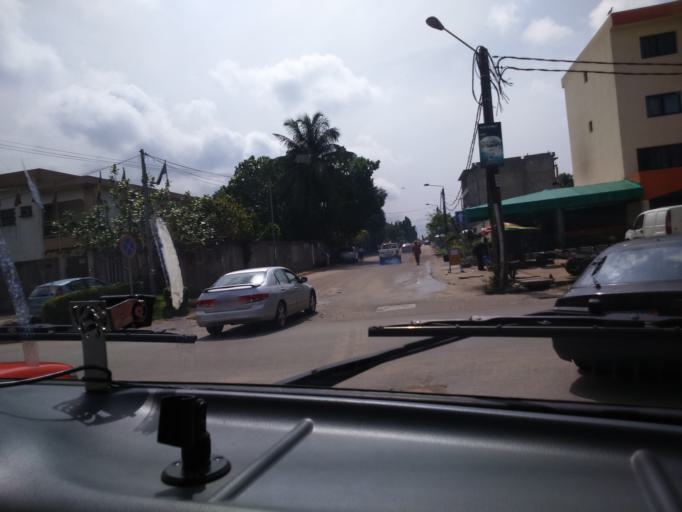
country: CI
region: Lagunes
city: Abidjan
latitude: 5.3559
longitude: -3.9778
